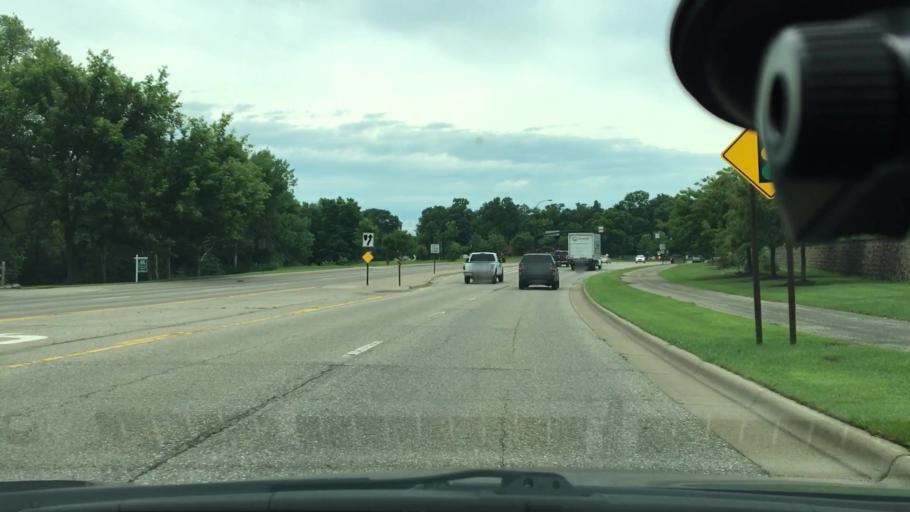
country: US
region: Minnesota
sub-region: Hennepin County
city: Maple Grove
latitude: 45.0683
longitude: -93.4312
